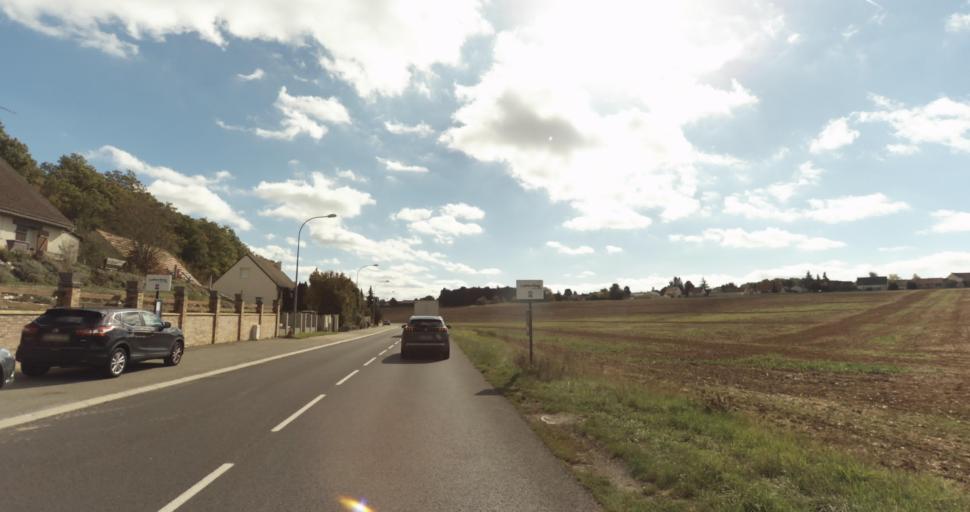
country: FR
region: Centre
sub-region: Departement d'Eure-et-Loir
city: Garnay
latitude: 48.7210
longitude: 1.3319
